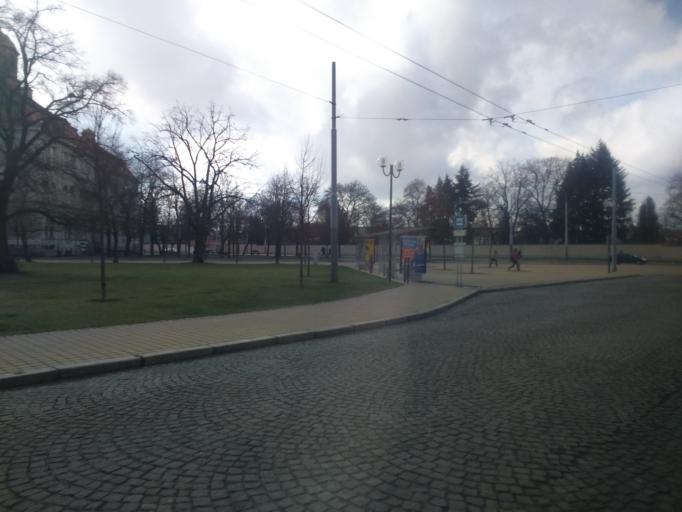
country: CZ
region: Plzensky
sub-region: Okres Plzen-Mesto
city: Pilsen
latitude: 49.7405
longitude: 13.3876
